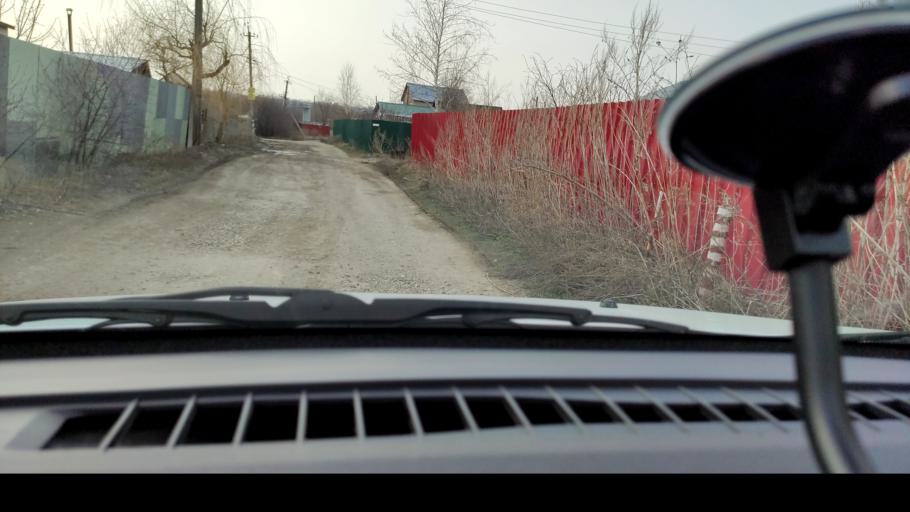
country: RU
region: Samara
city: Smyshlyayevka
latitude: 53.0916
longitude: 50.3939
